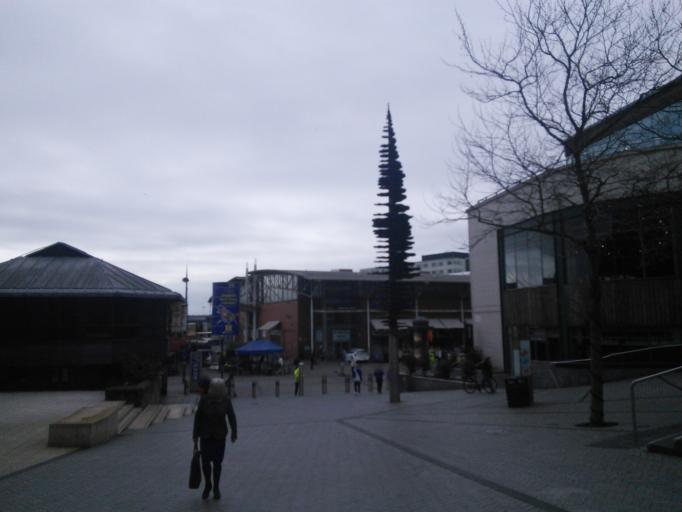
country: GB
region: England
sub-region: City and Borough of Birmingham
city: Birmingham
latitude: 52.4771
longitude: -1.8937
